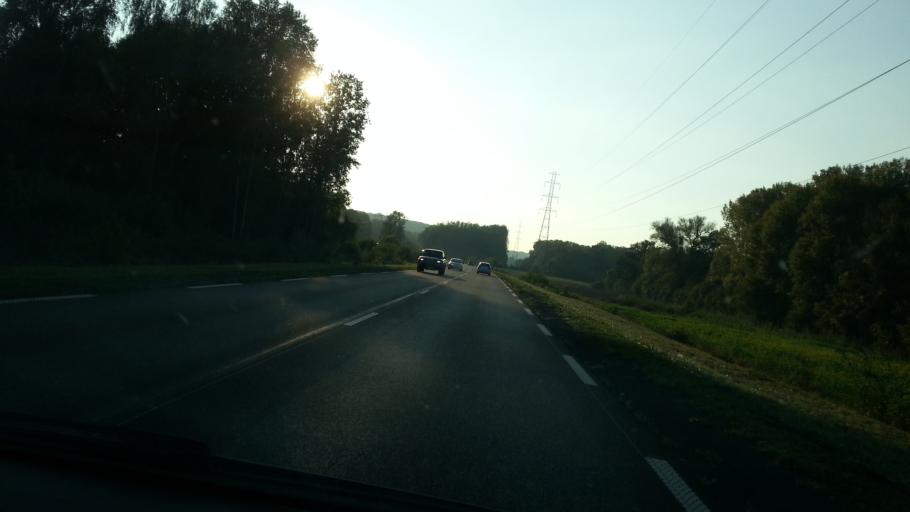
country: FR
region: Picardie
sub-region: Departement de l'Oise
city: Brenouille
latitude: 49.3174
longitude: 2.5687
